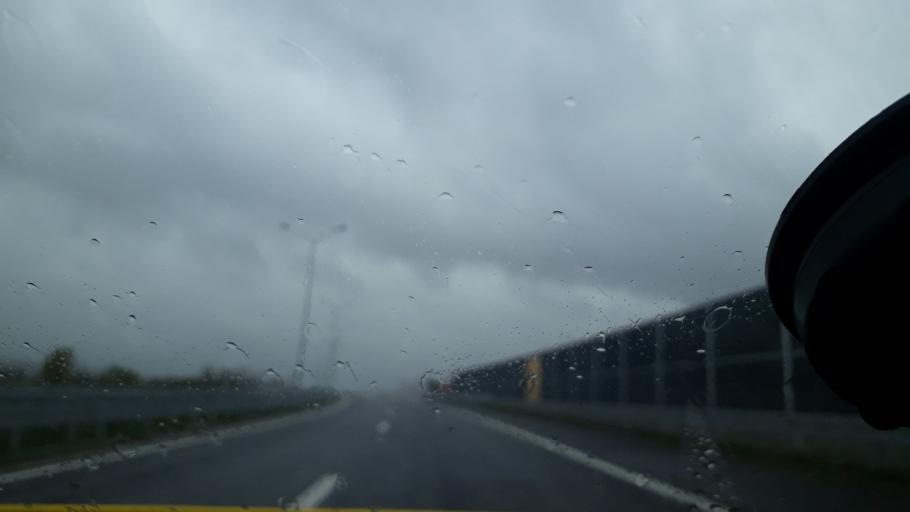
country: BA
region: Republika Srpska
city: Maglajani
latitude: 44.9135
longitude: 17.3408
